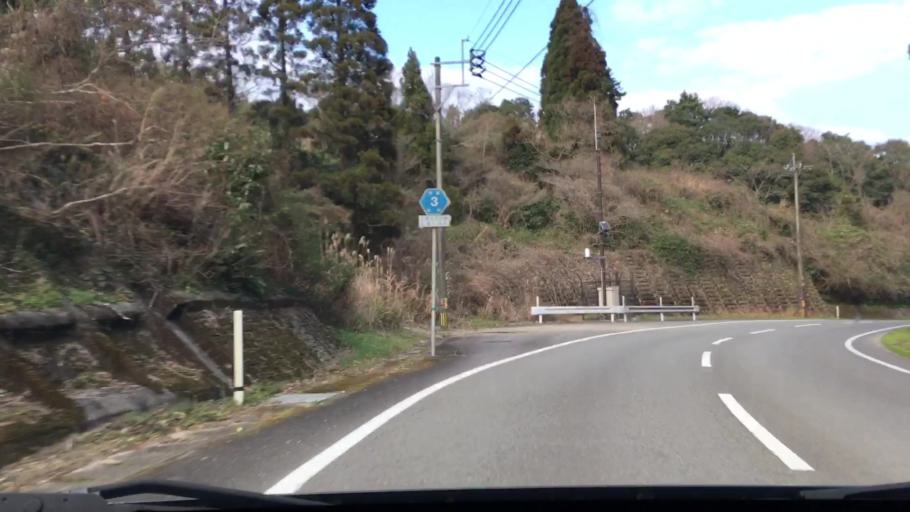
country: JP
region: Miyazaki
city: Kushima
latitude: 31.5761
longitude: 131.2688
